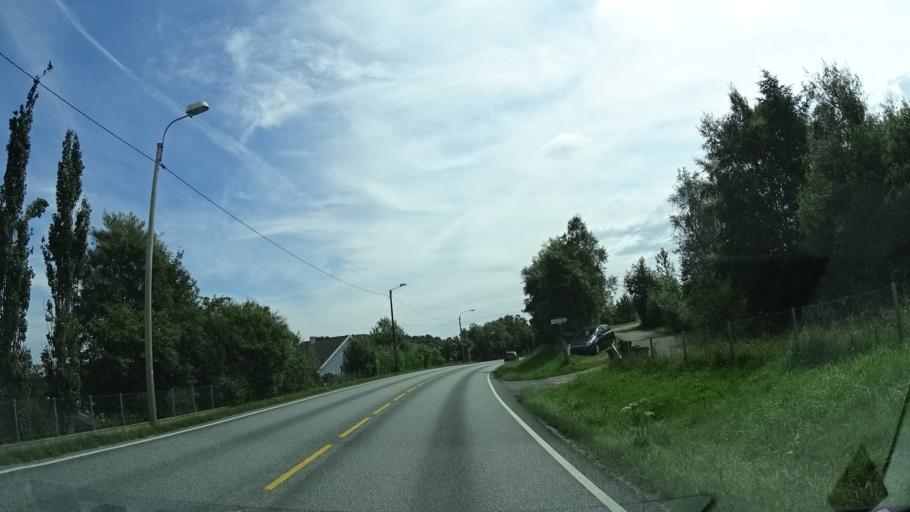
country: NO
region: Rogaland
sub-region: Randaberg
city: Randaberg
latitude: 58.9889
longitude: 5.6630
